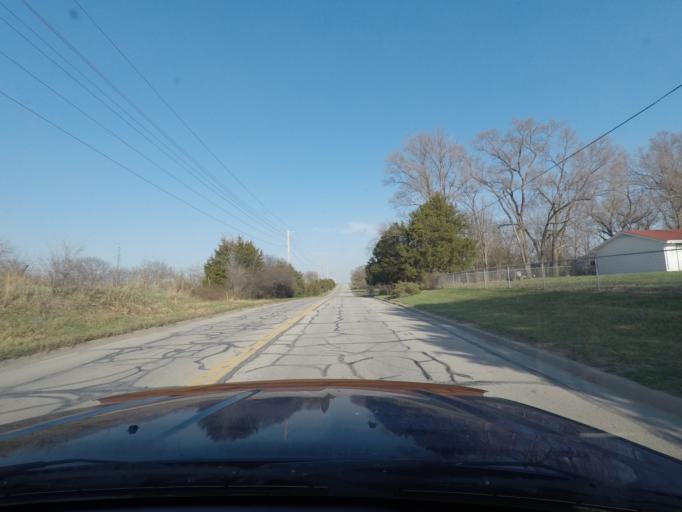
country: US
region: Kansas
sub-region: Douglas County
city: Lawrence
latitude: 39.0006
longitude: -95.2779
